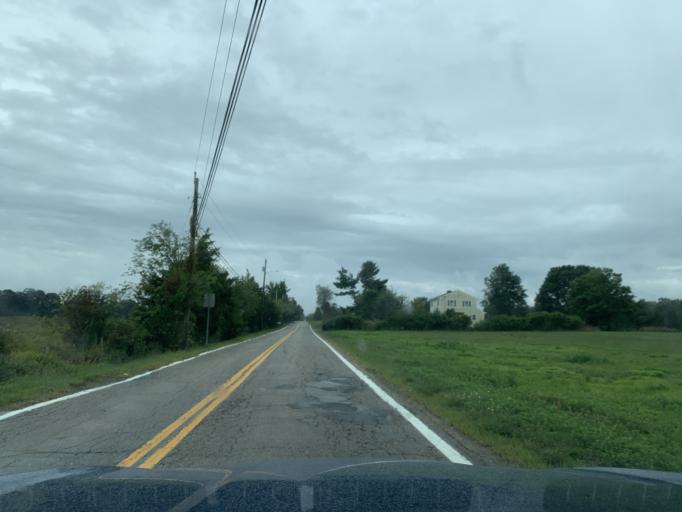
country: US
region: Rhode Island
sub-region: Bristol County
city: Warren
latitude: 41.7487
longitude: -71.2657
